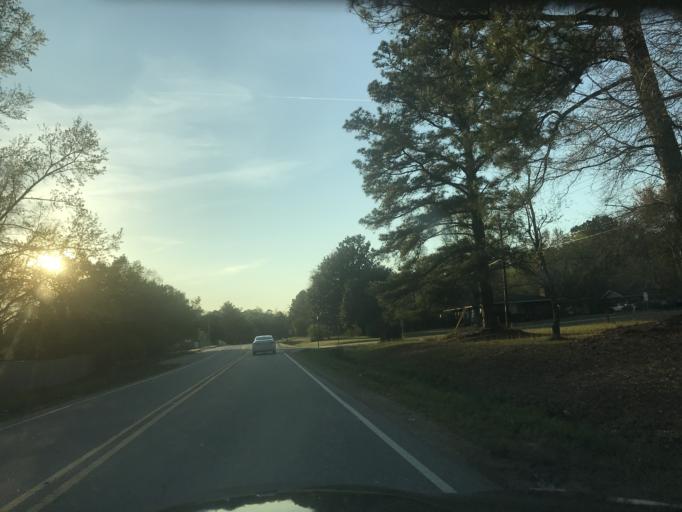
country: US
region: North Carolina
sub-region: Wake County
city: Knightdale
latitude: 35.7571
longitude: -78.5440
